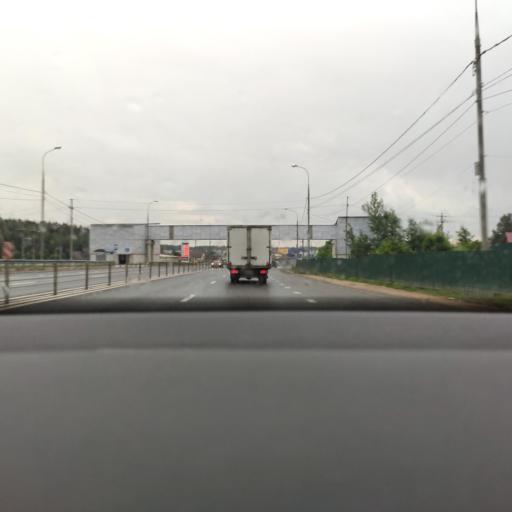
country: RU
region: Moskovskaya
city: Marfino
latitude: 56.0547
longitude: 37.5308
